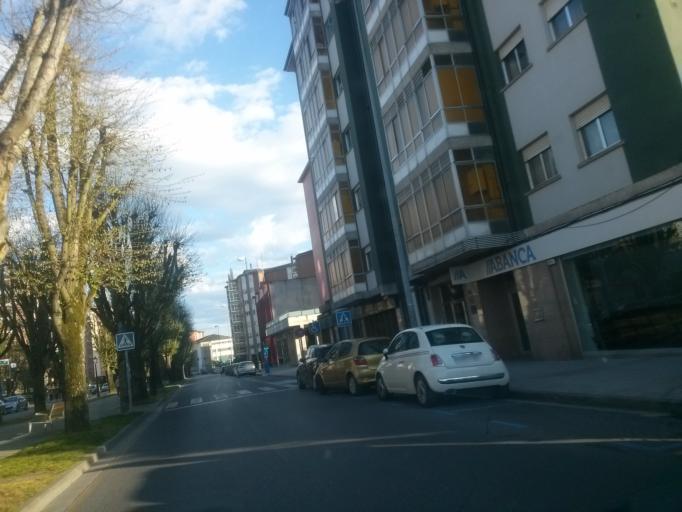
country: ES
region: Galicia
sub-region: Provincia de Lugo
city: Lugo
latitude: 43.0049
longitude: -7.5548
